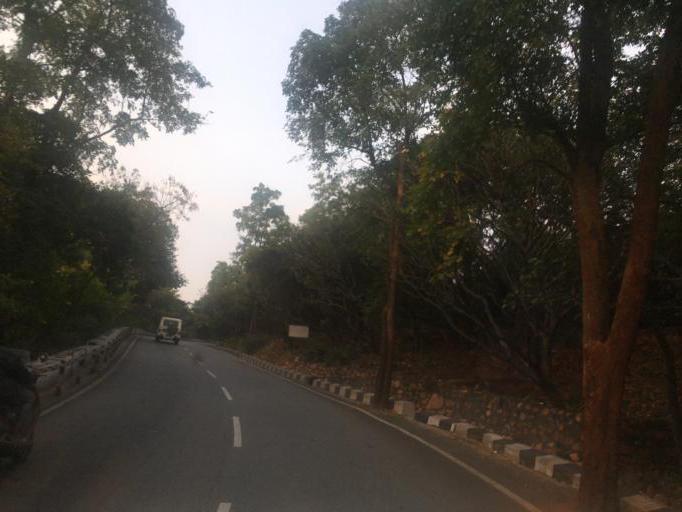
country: IN
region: Andhra Pradesh
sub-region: Chittoor
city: Akkarampalle
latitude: 13.6468
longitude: 79.3913
